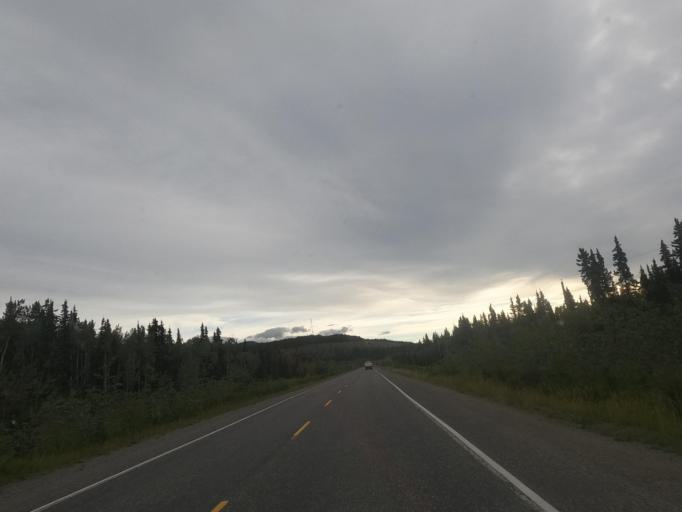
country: CA
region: Yukon
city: Whitehorse
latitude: 60.7588
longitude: -136.1128
